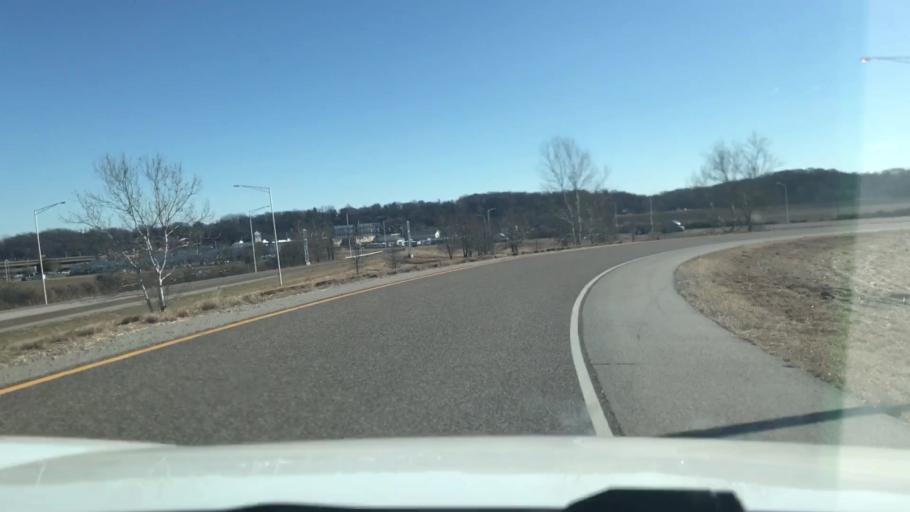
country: US
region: Illinois
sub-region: Saint Clair County
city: Caseyville
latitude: 38.6756
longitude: -90.0276
